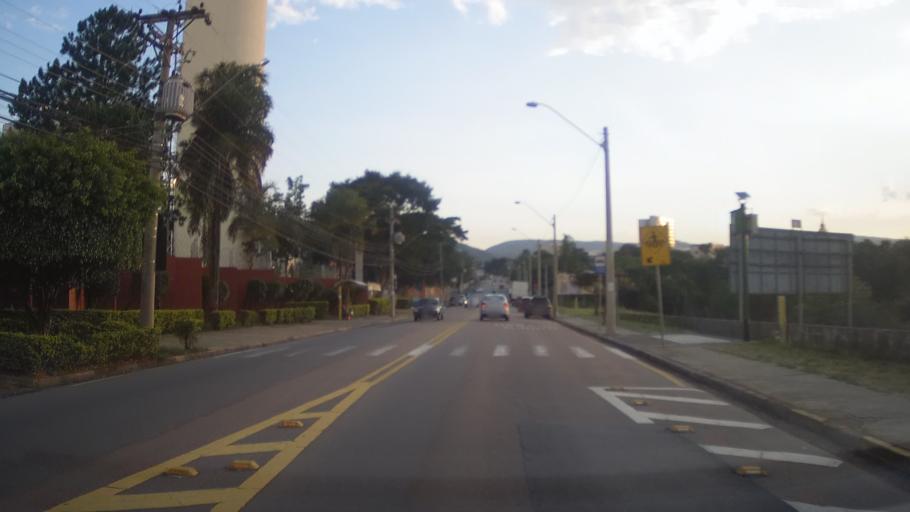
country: BR
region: Sao Paulo
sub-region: Jundiai
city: Jundiai
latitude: -23.1881
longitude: -46.9602
